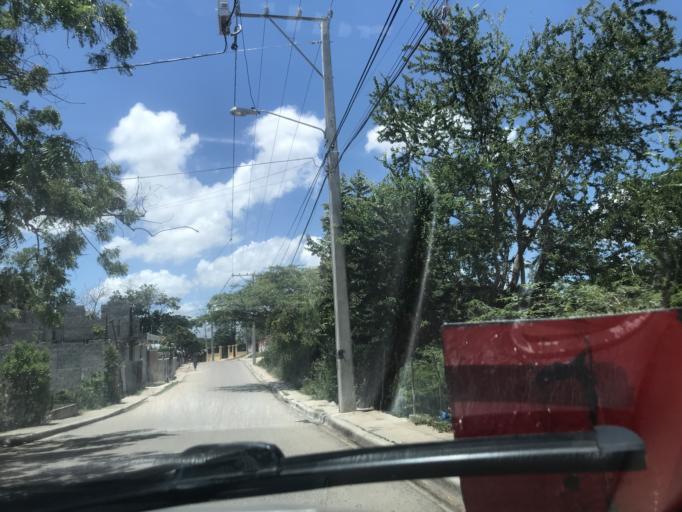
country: DO
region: Santiago
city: Santiago de los Caballeros
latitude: 19.4062
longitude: -70.6831
